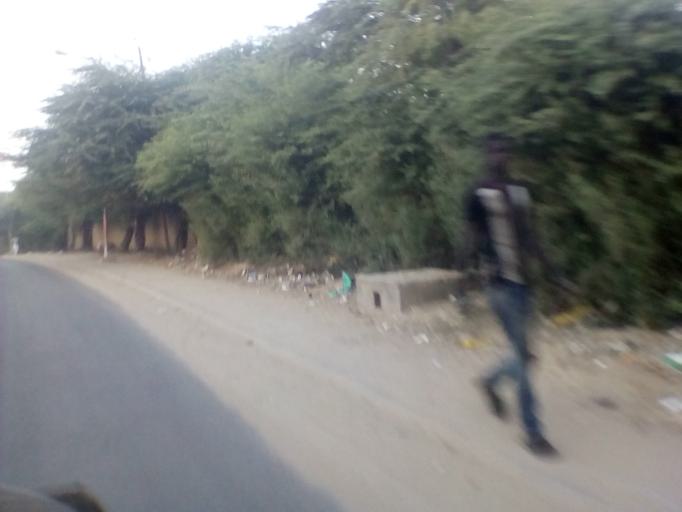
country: SN
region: Saint-Louis
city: Saint-Louis
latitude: 16.0142
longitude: -16.4890
